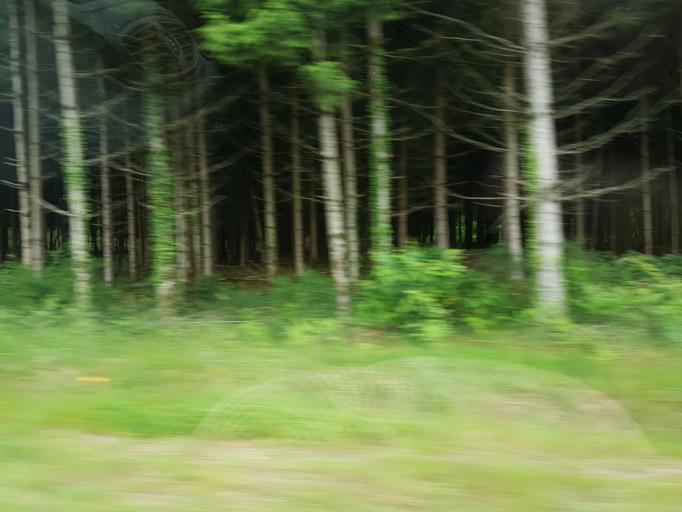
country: FR
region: Bourgogne
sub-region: Departement de la Nievre
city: Chateau-Chinon(Ville)
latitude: 47.0507
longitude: 3.9900
